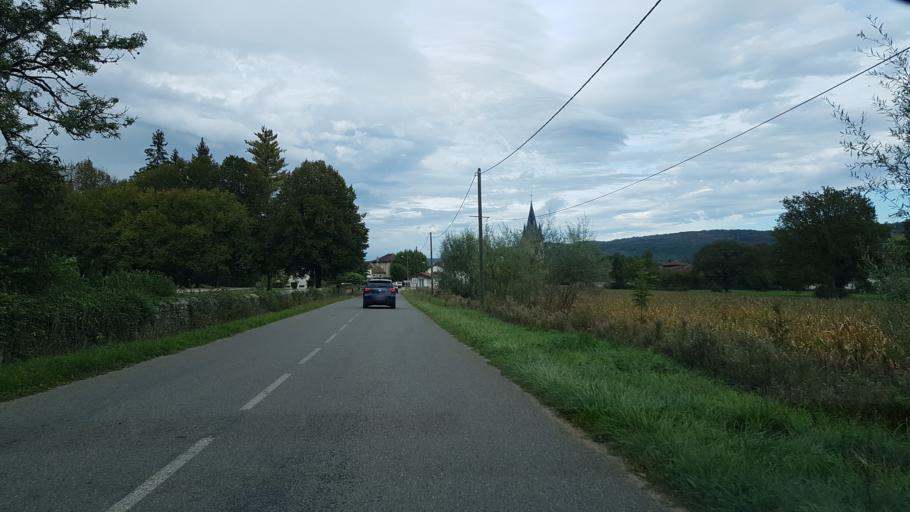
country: FR
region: Rhone-Alpes
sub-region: Departement de l'Ain
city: Villereversure
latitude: 46.1829
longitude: 5.3800
